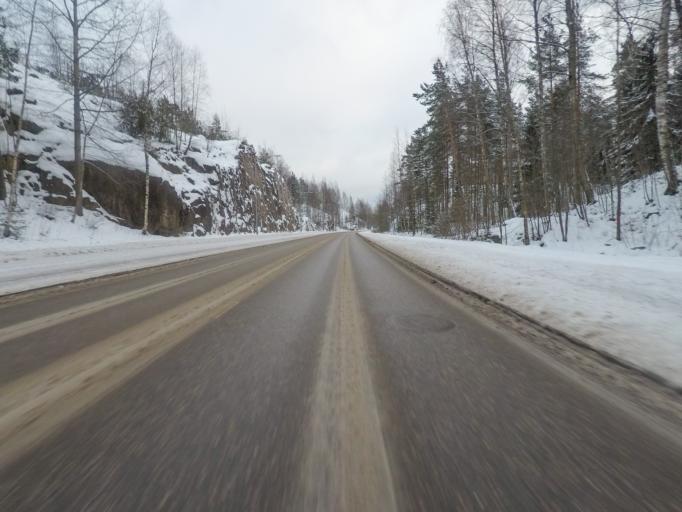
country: FI
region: Uusimaa
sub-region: Helsinki
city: Vantaa
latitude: 60.2171
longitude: 25.0544
